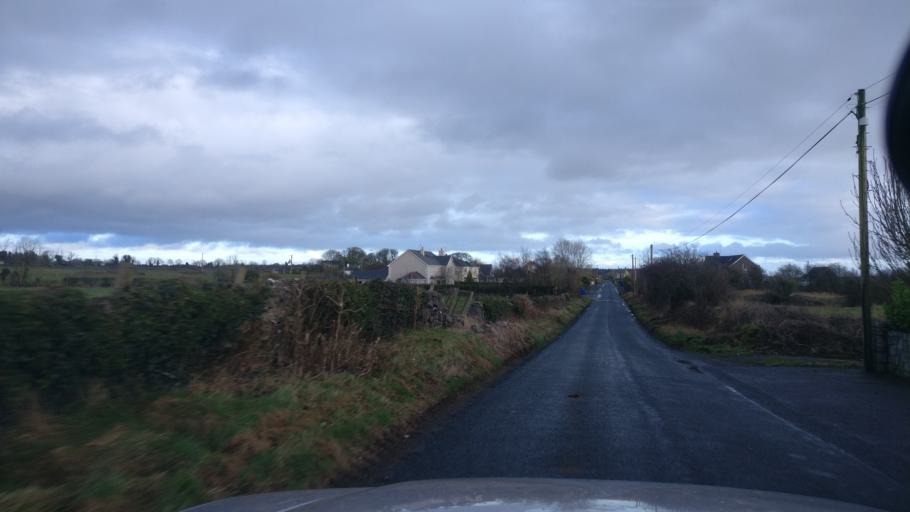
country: IE
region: Connaught
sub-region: County Galway
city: Athenry
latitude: 53.2957
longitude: -8.6888
